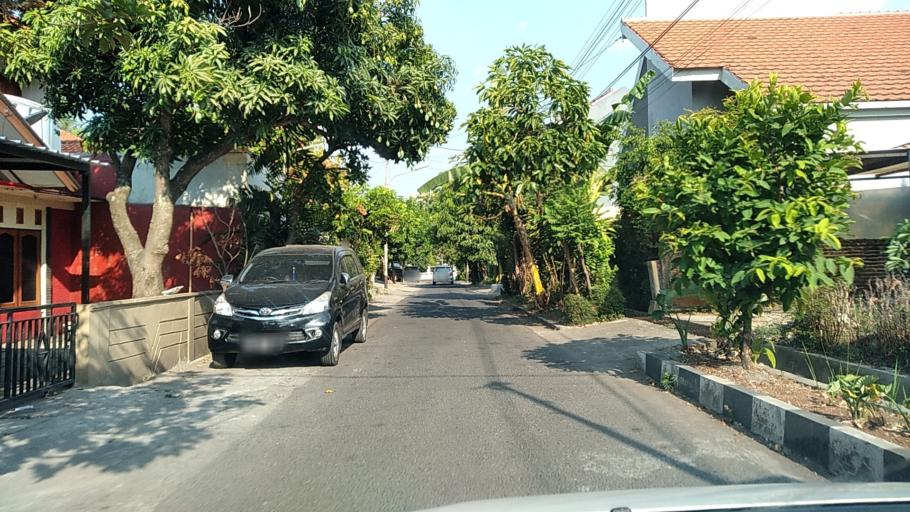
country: ID
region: Central Java
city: Ungaran
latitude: -7.0695
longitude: 110.4265
